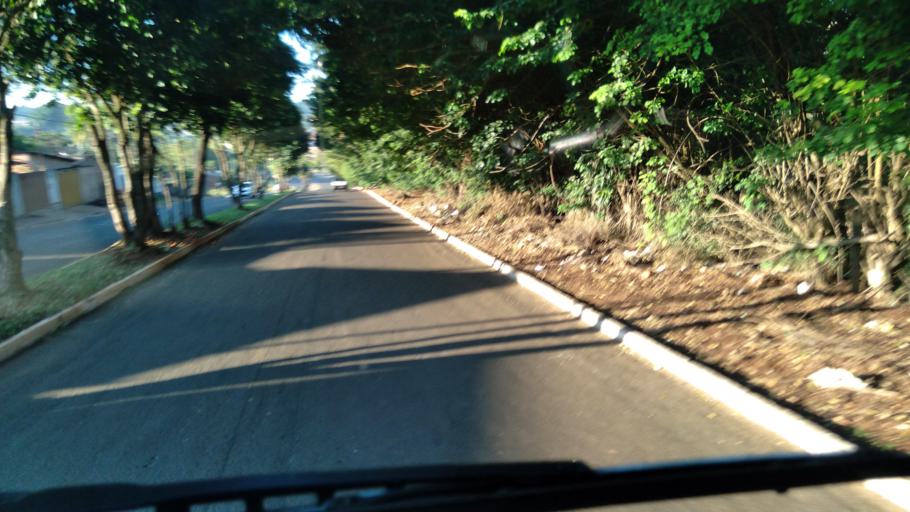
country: BR
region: Goias
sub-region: Mineiros
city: Mineiros
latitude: -17.5764
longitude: -52.5665
